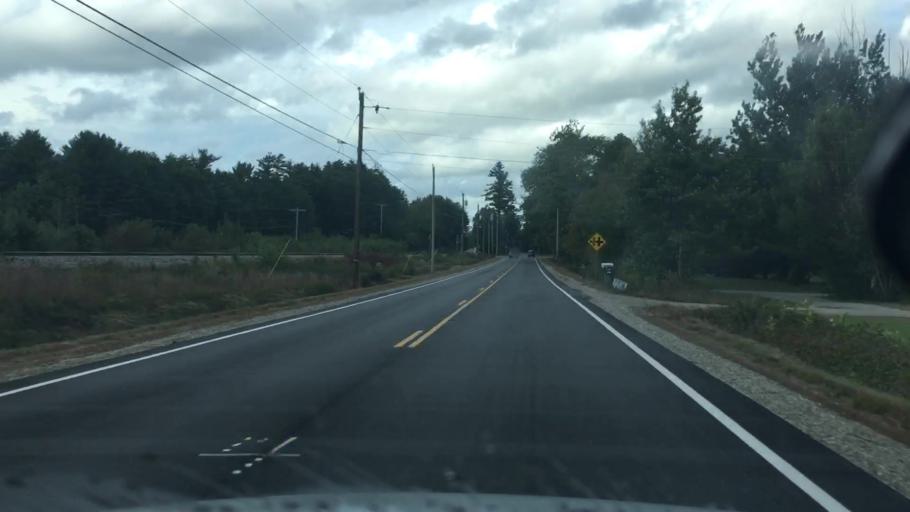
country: US
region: New Hampshire
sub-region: Carroll County
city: Sanbornville
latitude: 43.5426
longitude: -71.0273
